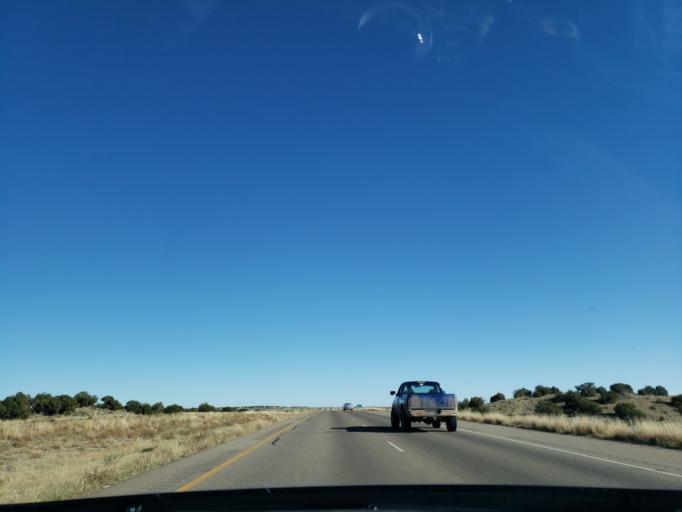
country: US
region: Colorado
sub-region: Fremont County
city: Florence
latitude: 38.4462
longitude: -105.1486
